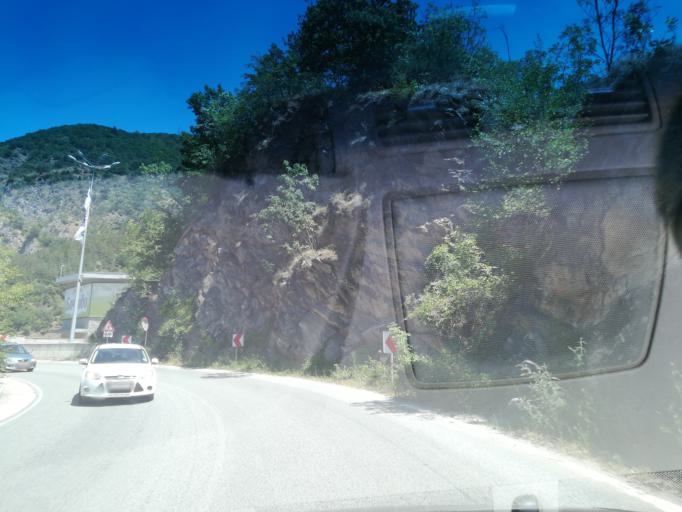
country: BG
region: Plovdiv
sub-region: Obshtina Luki
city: Luki
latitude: 41.9309
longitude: 24.8484
